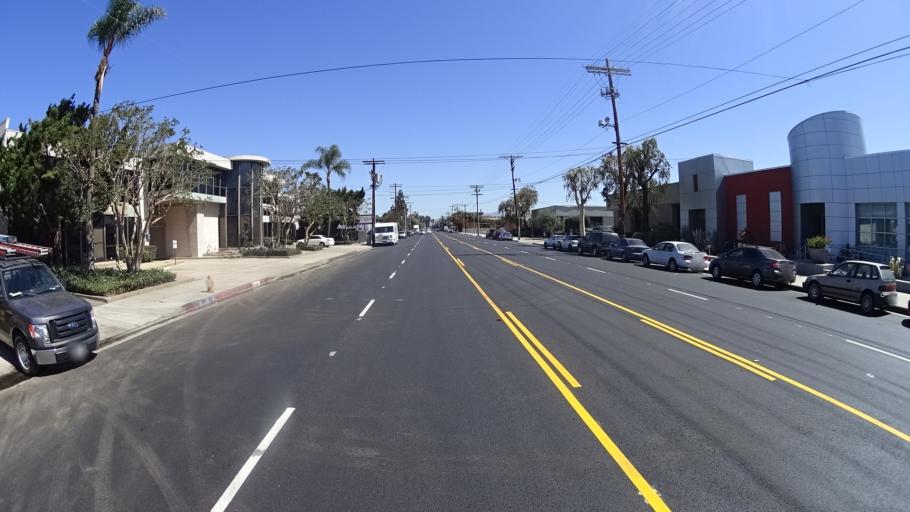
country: US
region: California
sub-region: Los Angeles County
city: Van Nuys
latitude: 34.1957
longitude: -118.4925
